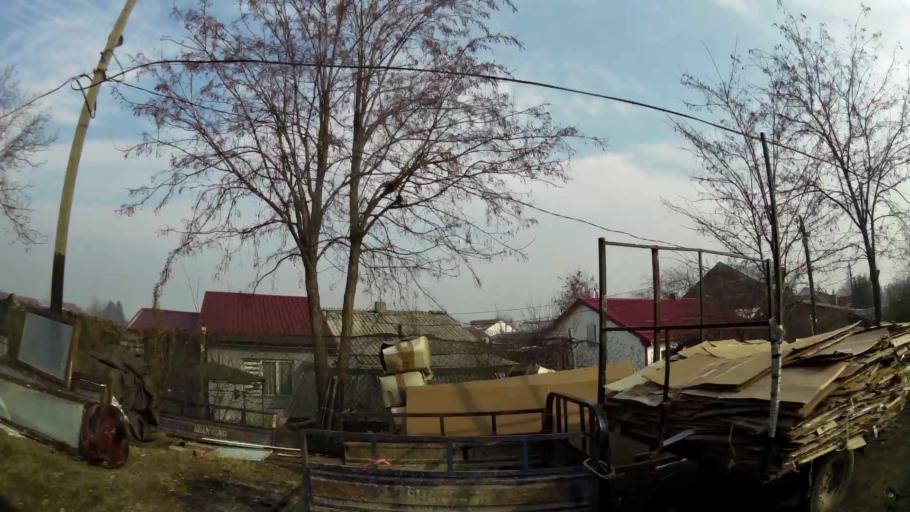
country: MK
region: Kisela Voda
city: Kisela Voda
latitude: 41.9854
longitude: 21.5009
